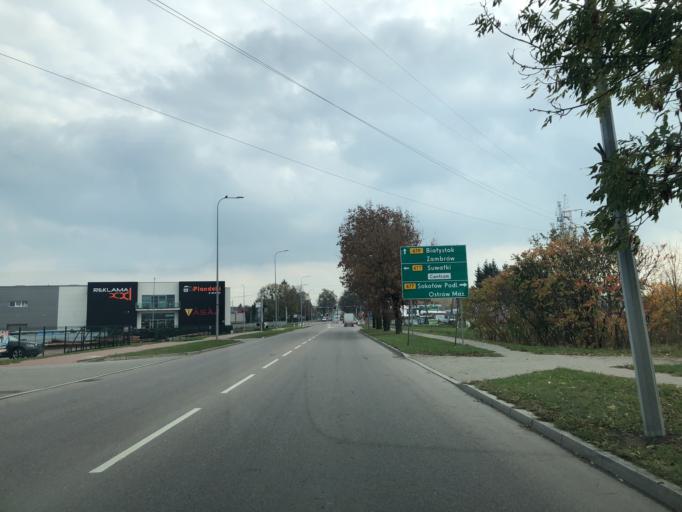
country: PL
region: Podlasie
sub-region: Lomza
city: Lomza
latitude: 53.1576
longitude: 22.0493
